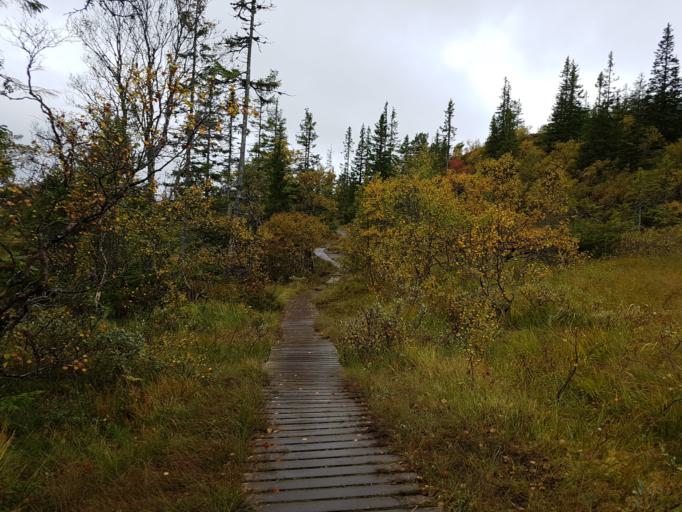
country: NO
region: Sor-Trondelag
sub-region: Melhus
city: Melhus
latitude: 63.4112
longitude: 10.2101
